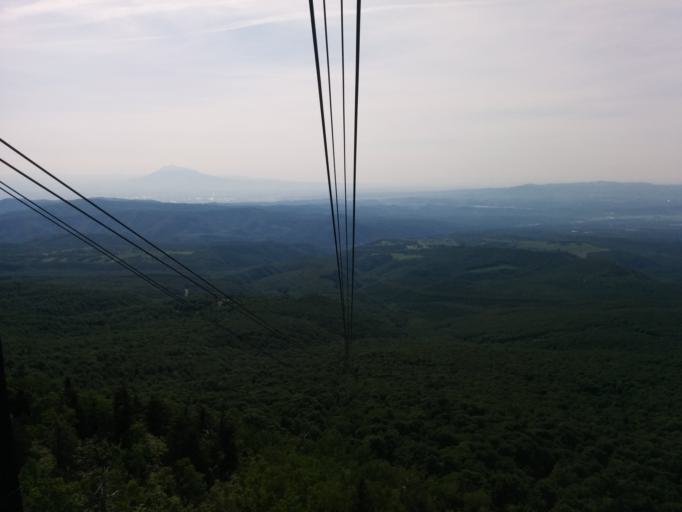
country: JP
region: Aomori
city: Aomori Shi
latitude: 40.6768
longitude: 140.8542
